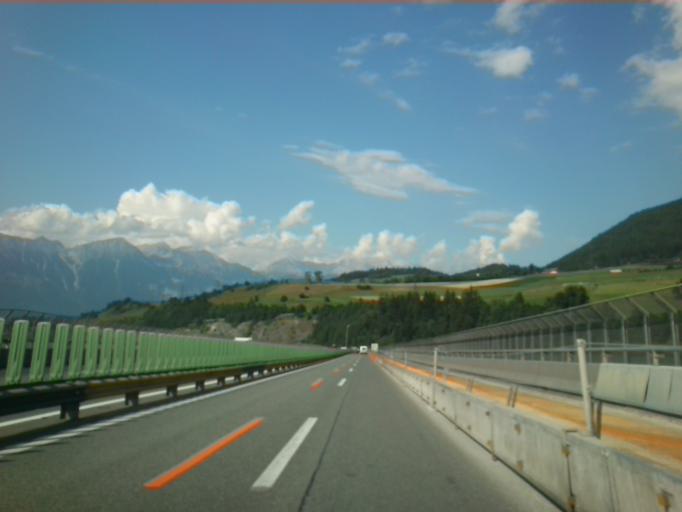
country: AT
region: Tyrol
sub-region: Politischer Bezirk Innsbruck Land
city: Patsch
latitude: 47.2011
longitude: 11.4013
